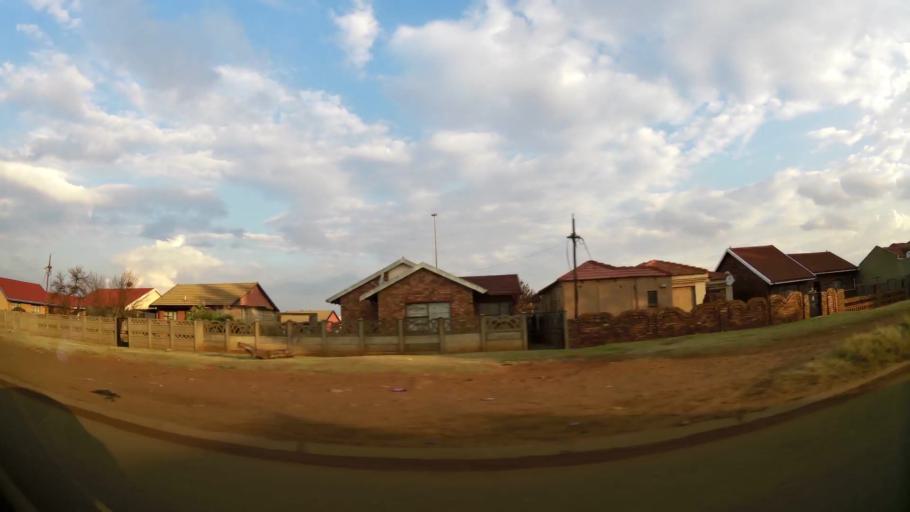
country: ZA
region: Gauteng
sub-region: City of Johannesburg Metropolitan Municipality
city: Orange Farm
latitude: -26.5935
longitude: 27.8400
